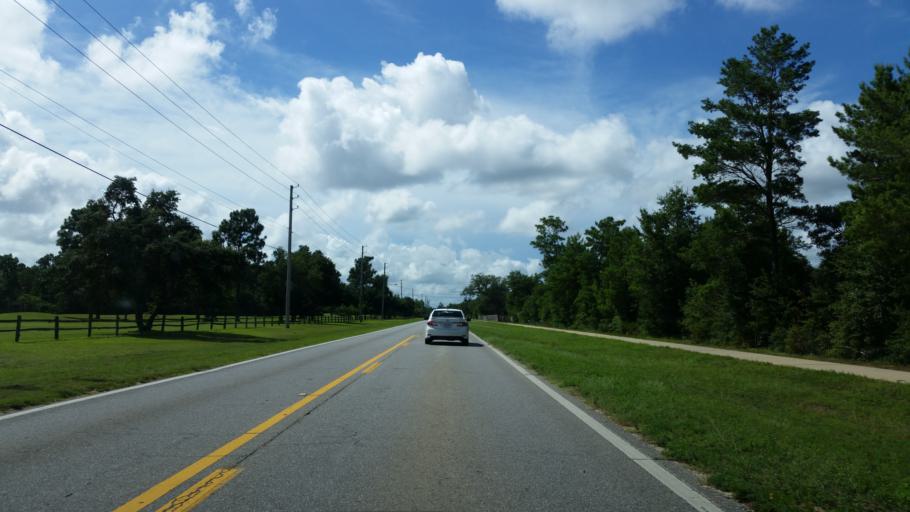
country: US
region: Florida
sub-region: Santa Rosa County
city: Holley
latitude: 30.4405
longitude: -86.9212
